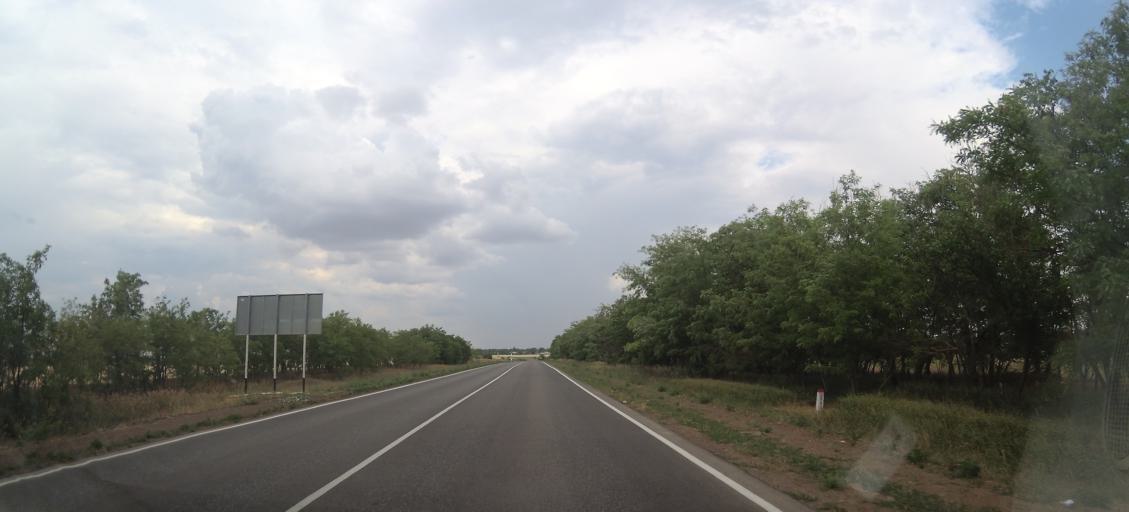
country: RU
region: Rostov
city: Gigant
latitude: 46.3437
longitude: 41.4175
